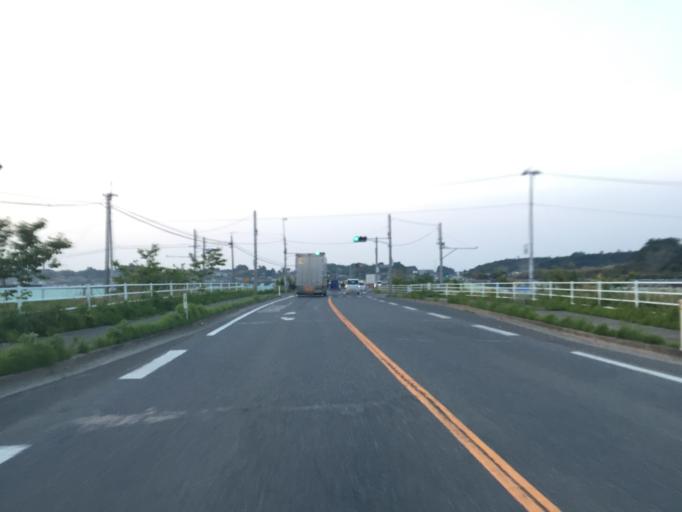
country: JP
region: Fukushima
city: Namie
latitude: 37.5974
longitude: 141.0033
